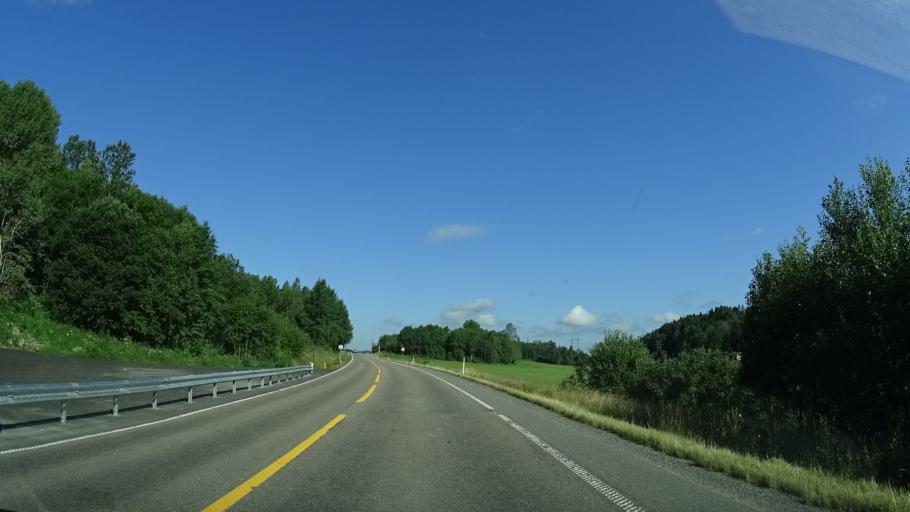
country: NO
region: Ostfold
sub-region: Hobol
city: Elvestad
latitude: 59.6653
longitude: 10.9052
